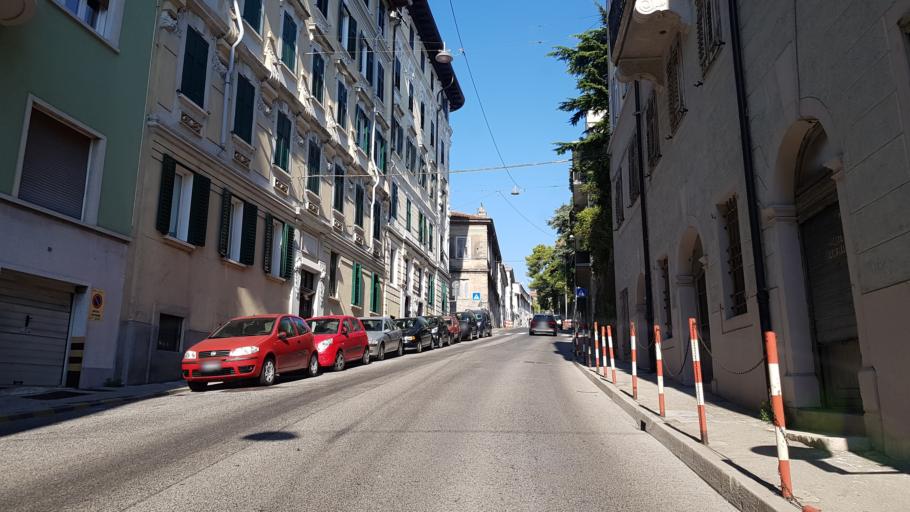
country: IT
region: Friuli Venezia Giulia
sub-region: Provincia di Trieste
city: Trieste
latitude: 45.6591
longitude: 13.7750
